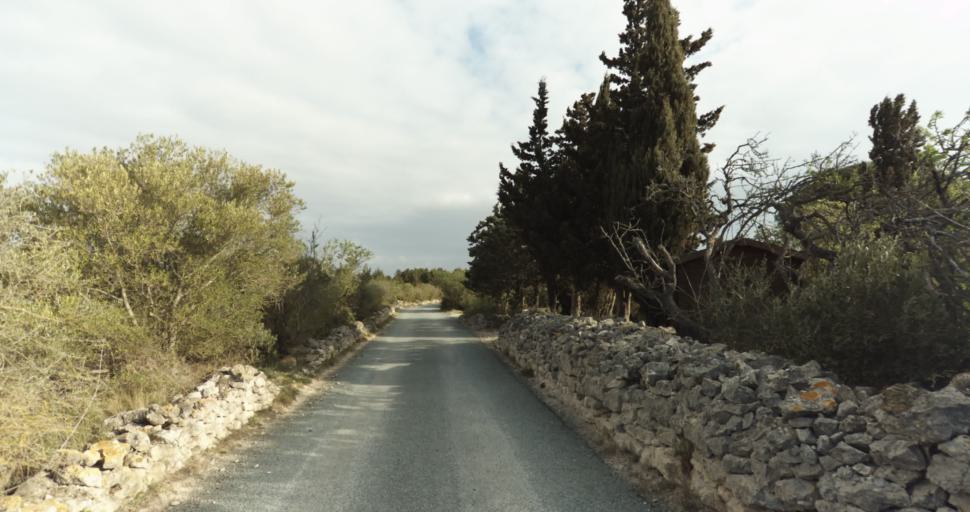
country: FR
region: Languedoc-Roussillon
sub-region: Departement de l'Aude
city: Leucate
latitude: 42.9132
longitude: 3.0246
